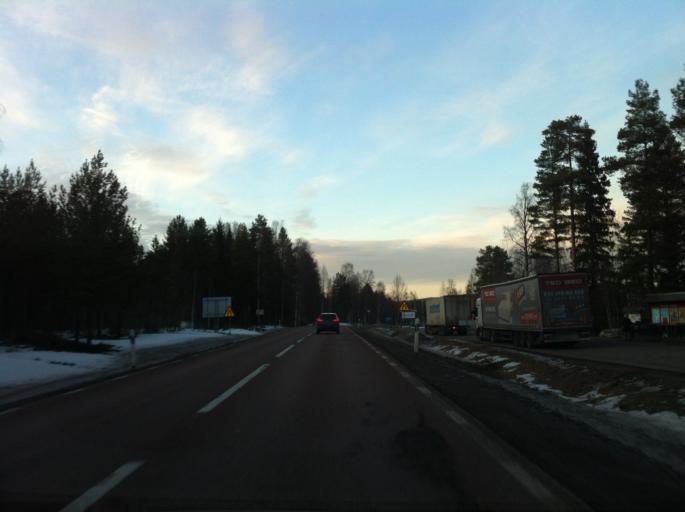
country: SE
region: Dalarna
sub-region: Vansbro Kommun
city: Vansbro
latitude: 60.8243
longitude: 14.1265
